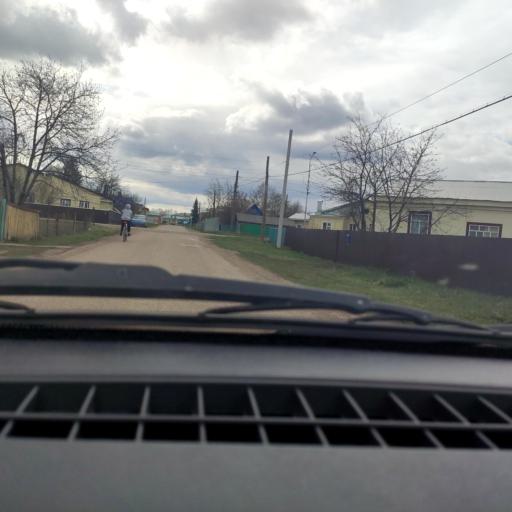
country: RU
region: Bashkortostan
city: Chekmagush
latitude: 55.1448
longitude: 54.6457
